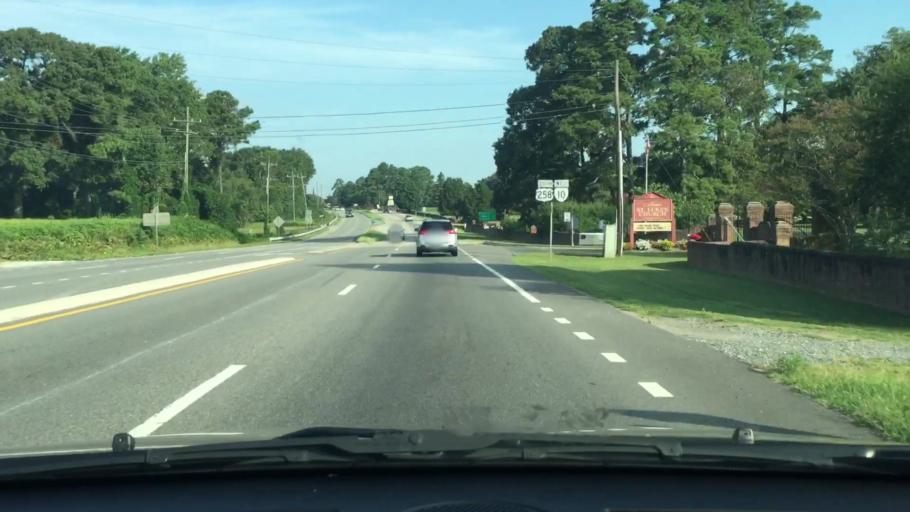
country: US
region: Virginia
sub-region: Isle of Wight County
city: Carrollton
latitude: 36.9387
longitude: -76.5869
